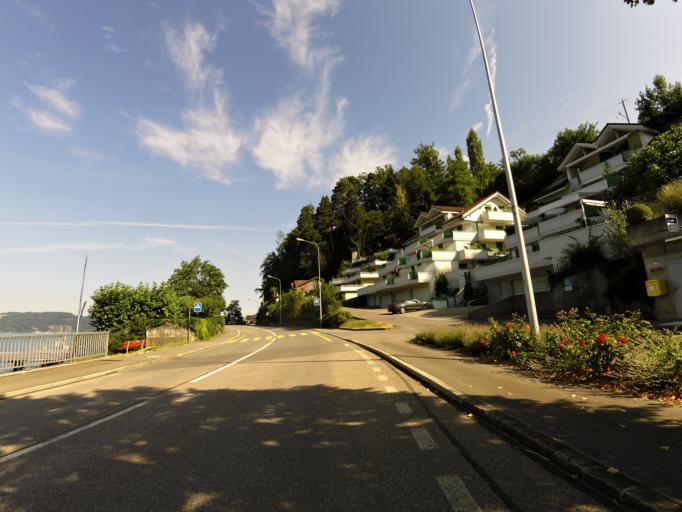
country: CH
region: Zug
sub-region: Zug
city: Walchwil
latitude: 47.0924
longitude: 8.5210
